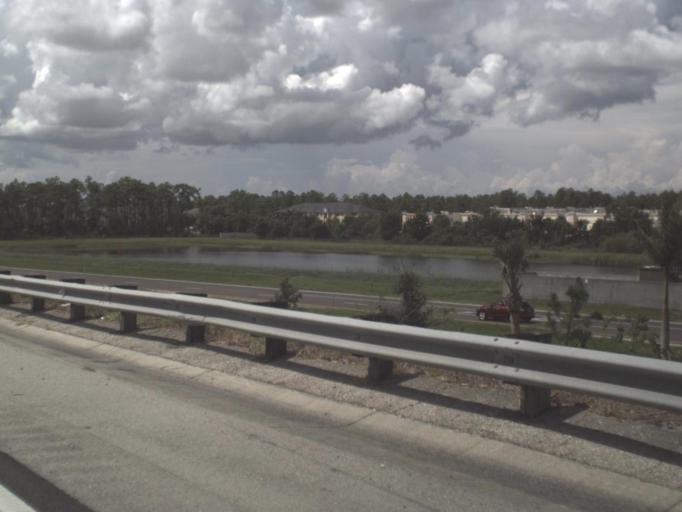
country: US
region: Florida
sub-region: Collier County
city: Vineyards
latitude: 26.2722
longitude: -81.7429
